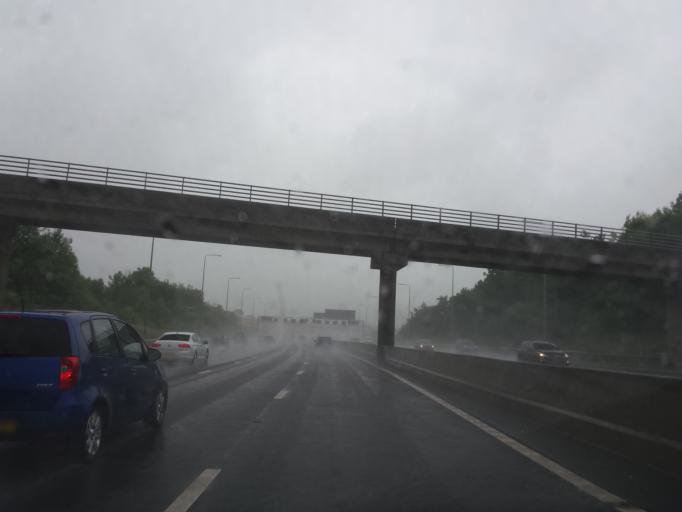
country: GB
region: England
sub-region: Nottinghamshire
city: Kimberley
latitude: 52.9757
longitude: -1.2526
